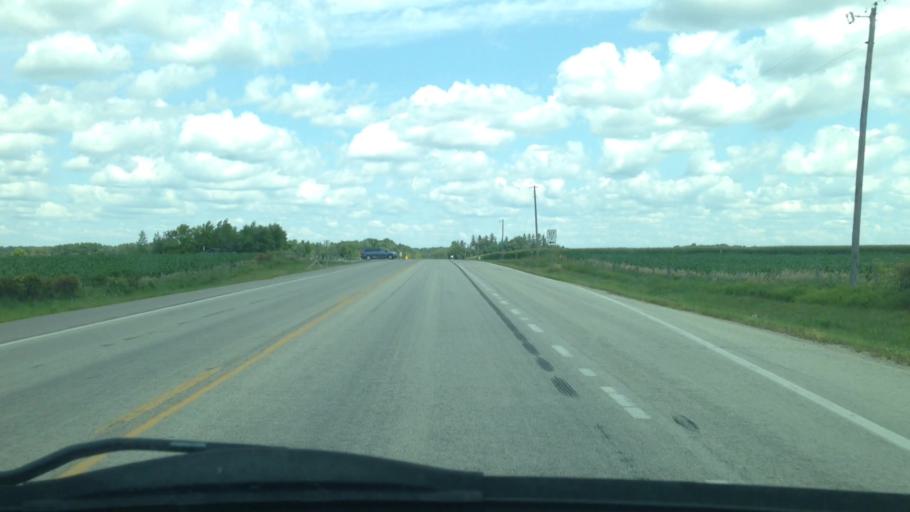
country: US
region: Minnesota
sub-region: Olmsted County
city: Rochester
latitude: 43.9630
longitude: -92.5183
